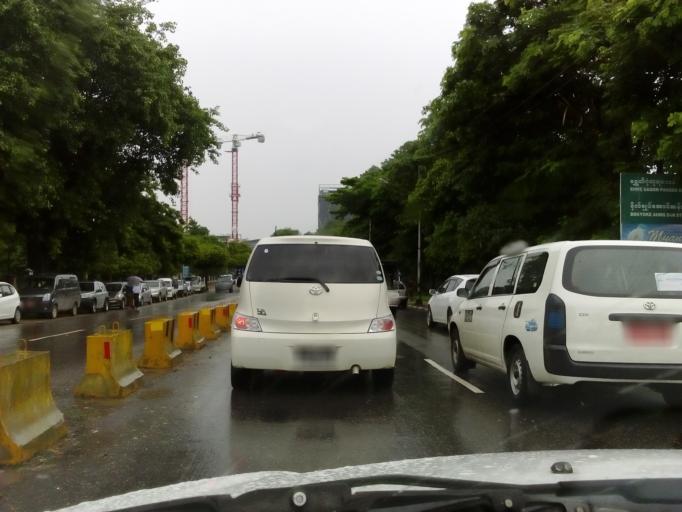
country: MM
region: Yangon
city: Yangon
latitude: 16.7813
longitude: 96.1533
